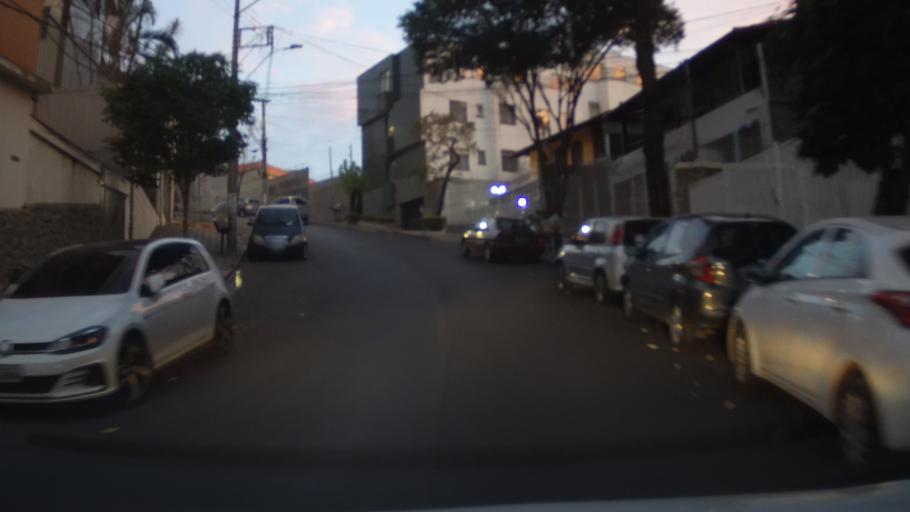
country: BR
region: Minas Gerais
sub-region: Belo Horizonte
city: Belo Horizonte
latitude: -19.8928
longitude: -43.9268
